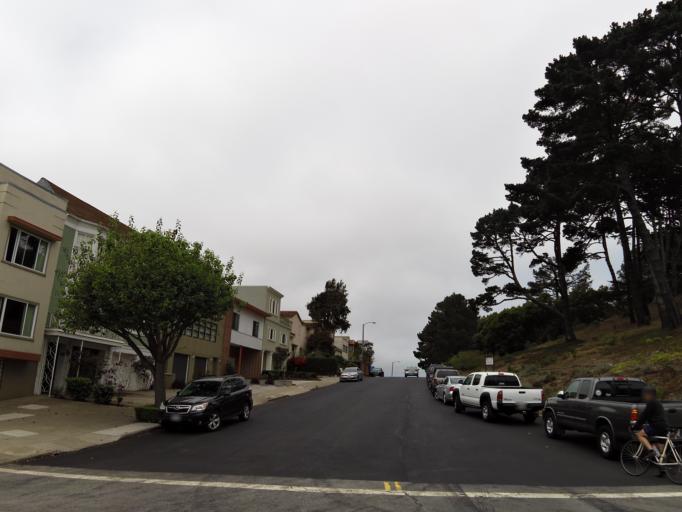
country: US
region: California
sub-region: San Francisco County
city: San Francisco
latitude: 37.7779
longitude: -122.4535
